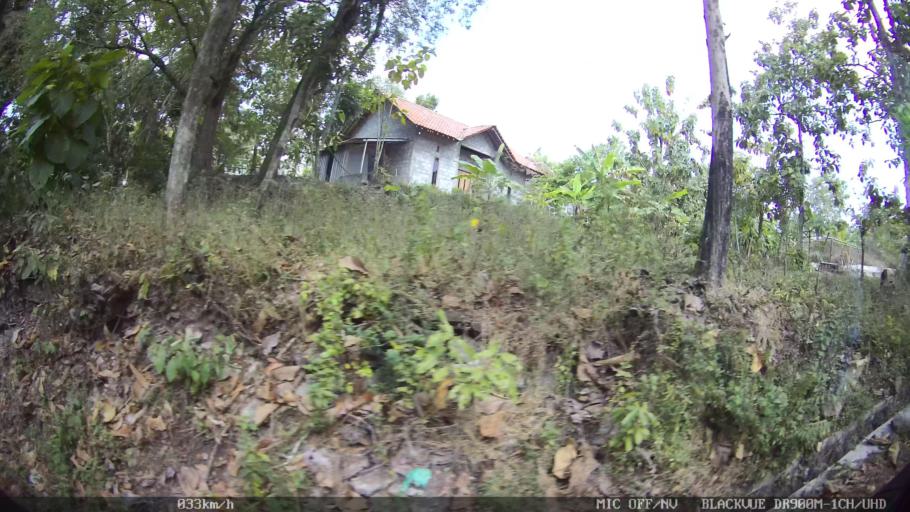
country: ID
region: Daerah Istimewa Yogyakarta
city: Kasihan
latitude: -7.8536
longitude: 110.3130
